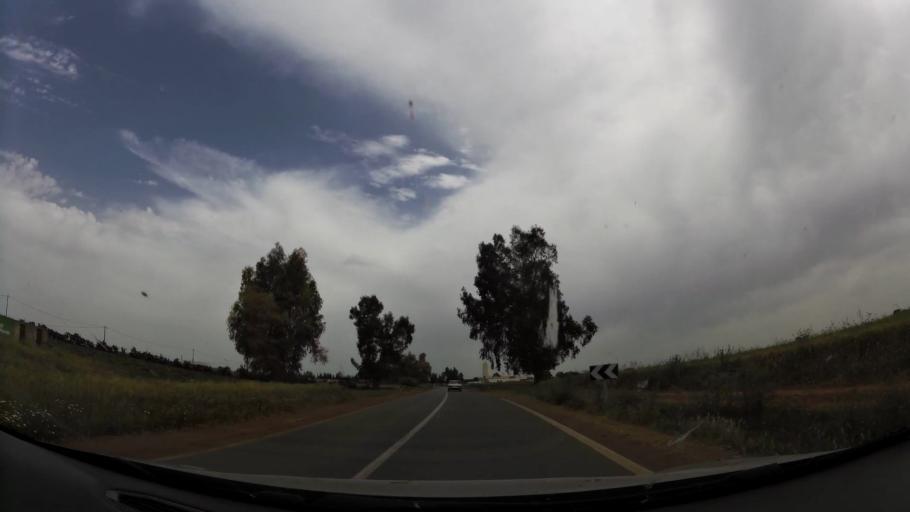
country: MA
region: Rabat-Sale-Zemmour-Zaer
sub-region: Khemisset
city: Tiflet
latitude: 33.8373
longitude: -6.2717
